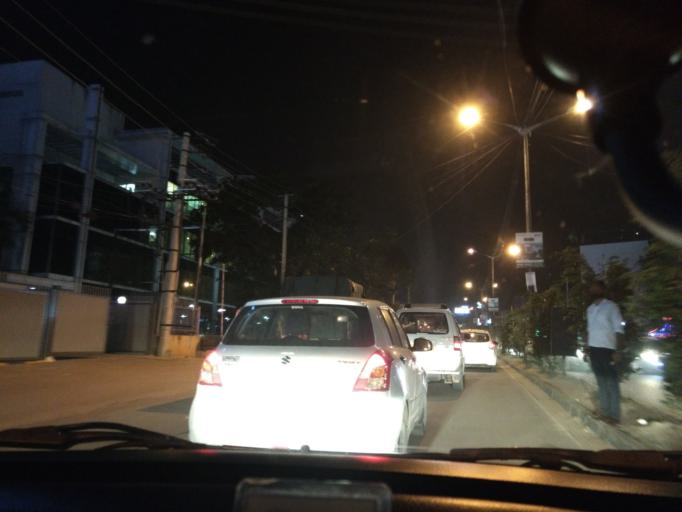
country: IN
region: Karnataka
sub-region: Bangalore Urban
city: Bangalore
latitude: 12.9177
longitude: 77.6718
